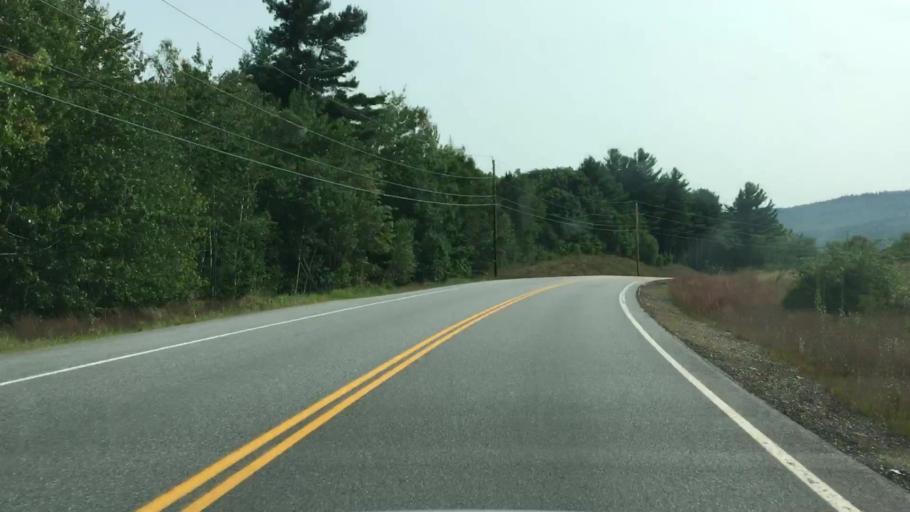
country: US
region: Maine
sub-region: Oxford County
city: Hebron
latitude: 44.2508
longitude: -70.4378
